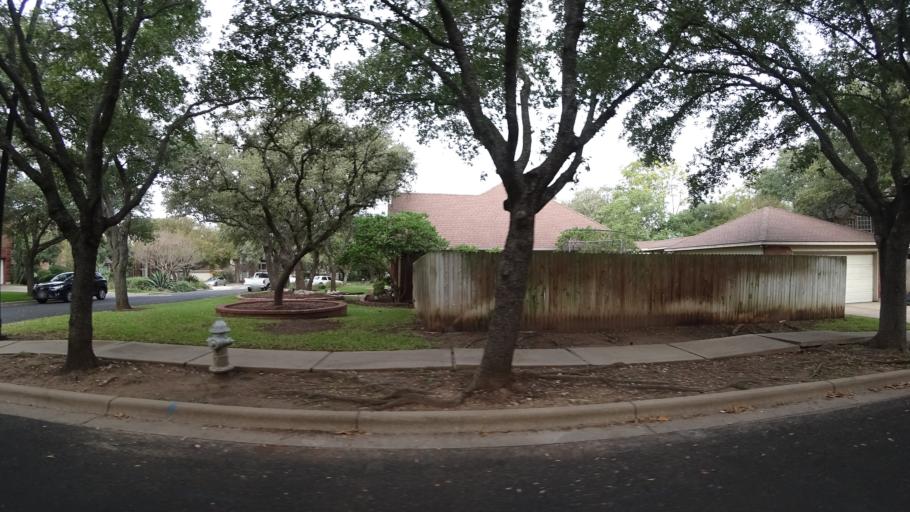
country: US
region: Texas
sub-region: Travis County
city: Shady Hollow
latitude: 30.1938
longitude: -97.8917
